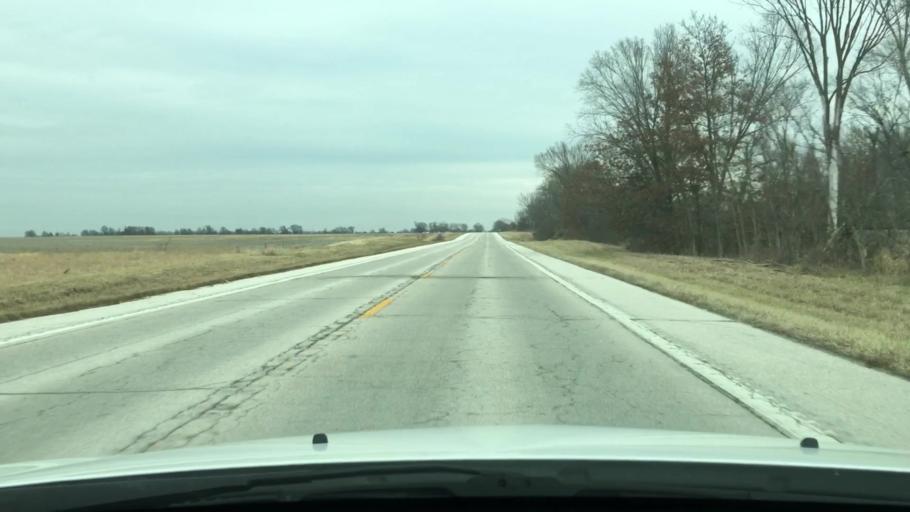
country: US
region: Missouri
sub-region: Audrain County
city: Vandalia
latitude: 39.3272
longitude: -91.4461
